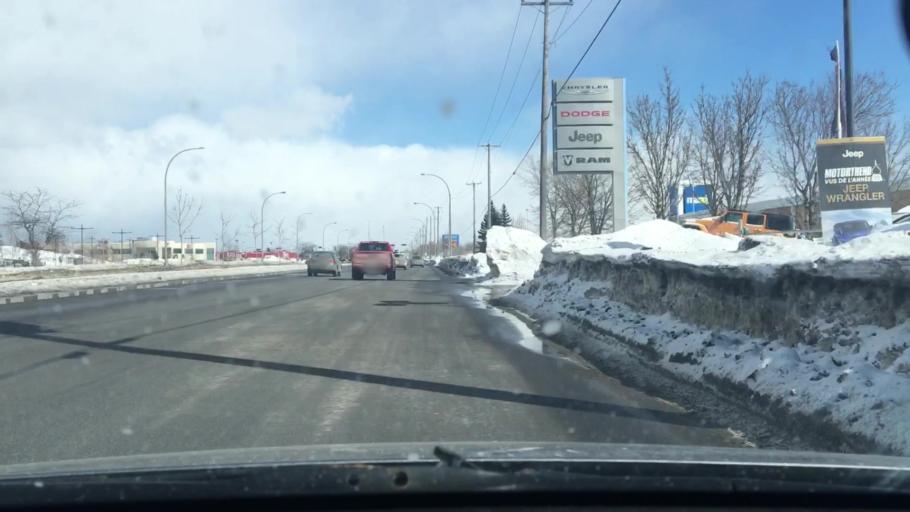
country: CA
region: Quebec
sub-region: Outaouais
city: Gatineau
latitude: 45.4806
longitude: -75.6840
